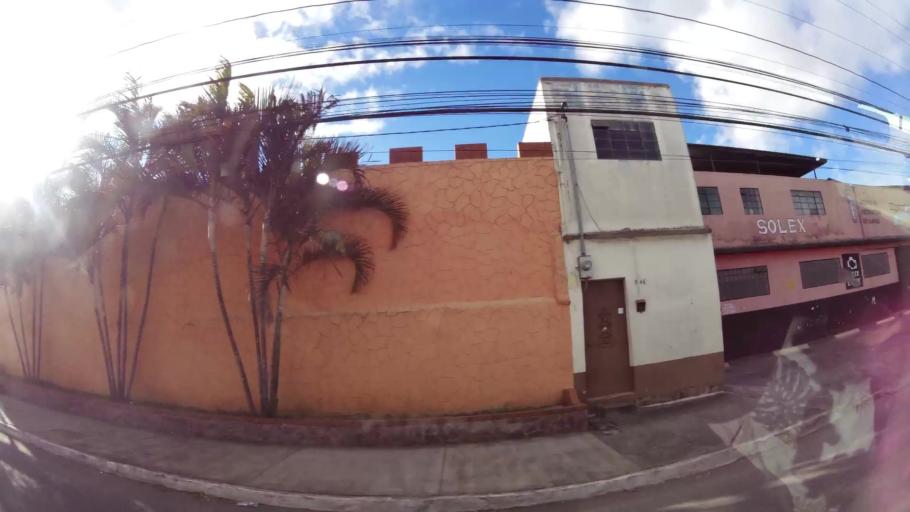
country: GT
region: Guatemala
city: Guatemala City
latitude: 14.6197
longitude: -90.5509
